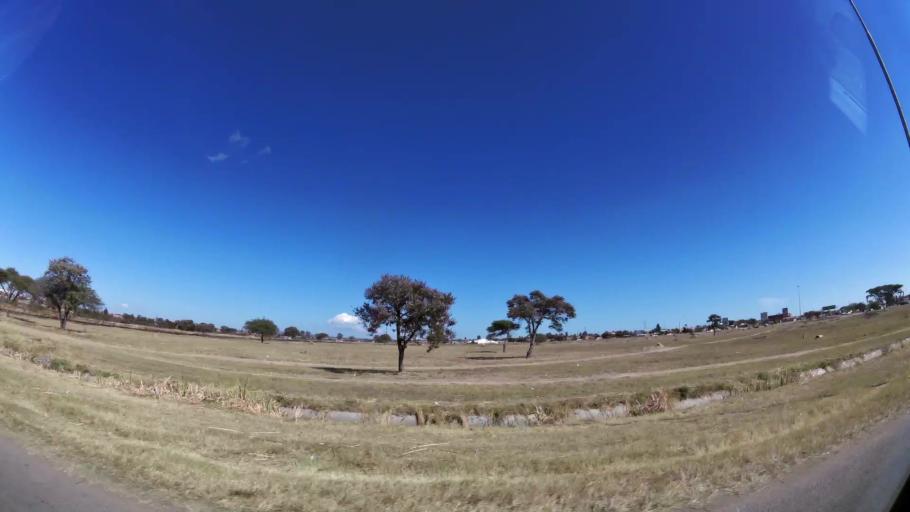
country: ZA
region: Limpopo
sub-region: Capricorn District Municipality
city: Polokwane
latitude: -23.8536
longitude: 29.4026
